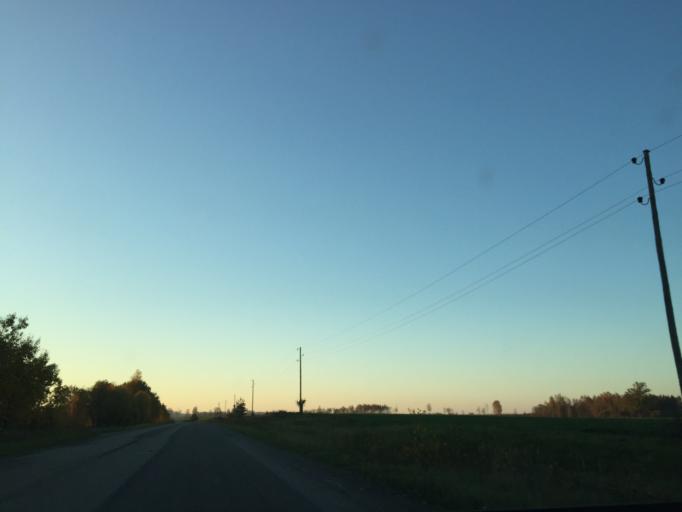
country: LT
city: Vieksniai
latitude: 56.3974
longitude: 22.5528
